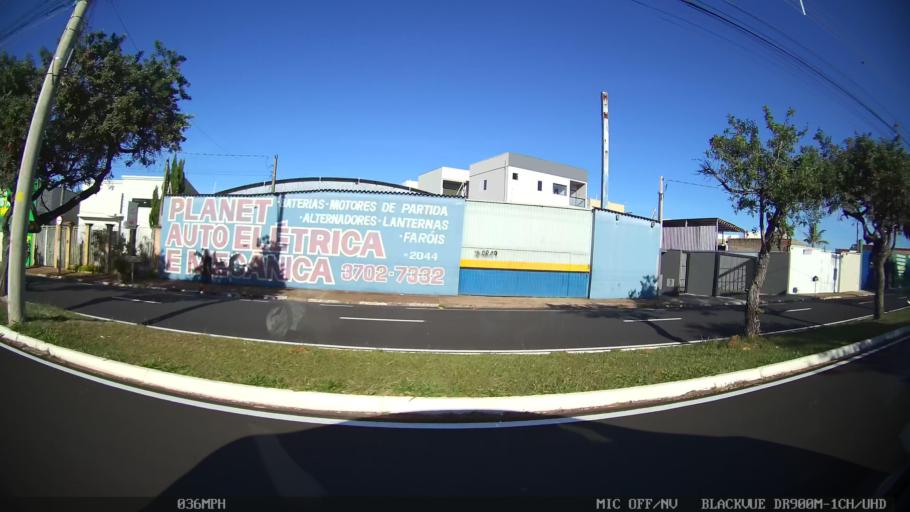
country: BR
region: Sao Paulo
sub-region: Franca
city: Franca
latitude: -20.5639
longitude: -47.3984
